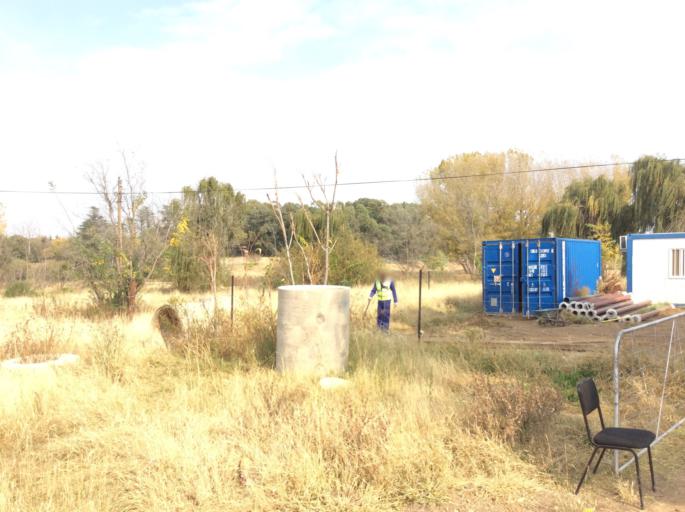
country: LS
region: Mafeteng
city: Mafeteng
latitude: -29.7276
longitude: 27.0337
